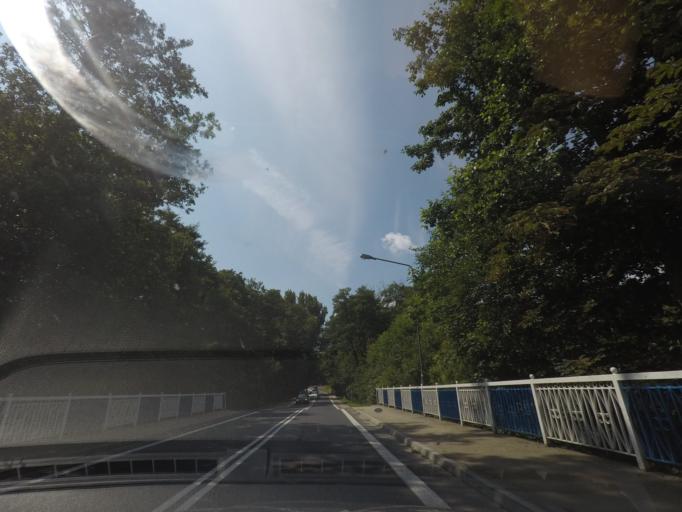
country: PL
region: West Pomeranian Voivodeship
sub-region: Powiat kolobrzeski
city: Dygowo
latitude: 54.1883
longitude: 15.6644
